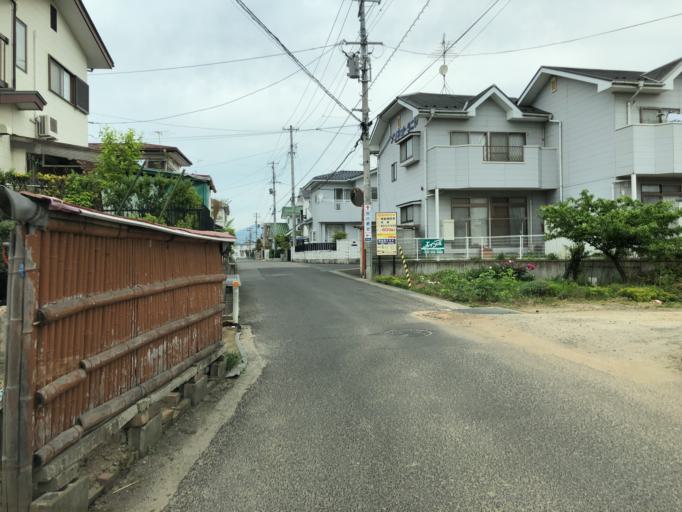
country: JP
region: Fukushima
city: Fukushima-shi
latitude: 37.7948
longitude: 140.4428
